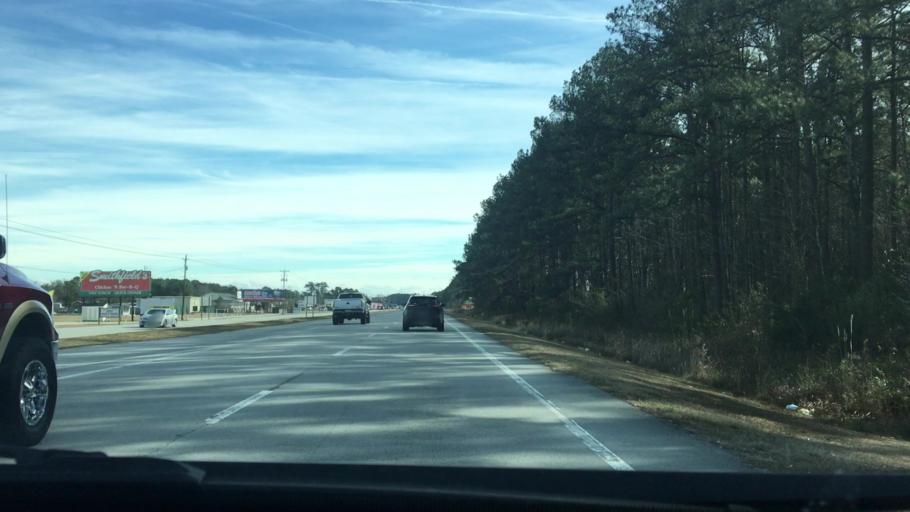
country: US
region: North Carolina
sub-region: Carteret County
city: Newport
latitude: 34.7580
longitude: -76.8498
